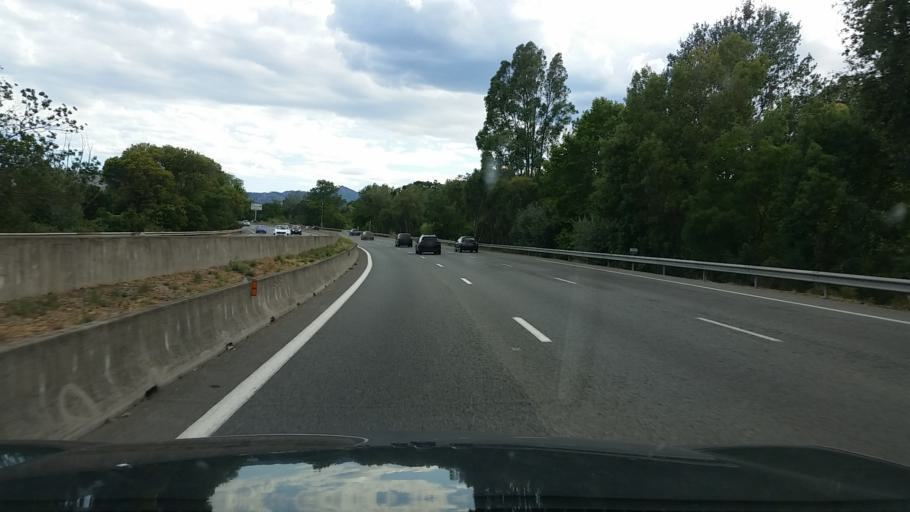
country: FR
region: Provence-Alpes-Cote d'Azur
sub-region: Departement des Alpes-Maritimes
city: Mandelieu-la-Napoule
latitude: 43.5564
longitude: 6.9467
